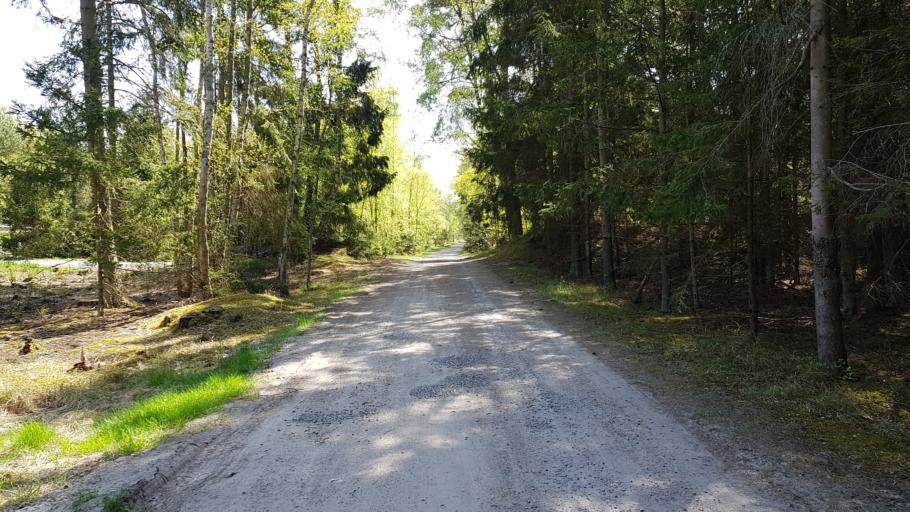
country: DK
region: Capital Region
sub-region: Bornholm Kommune
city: Nexo
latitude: 55.0005
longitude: 15.0816
